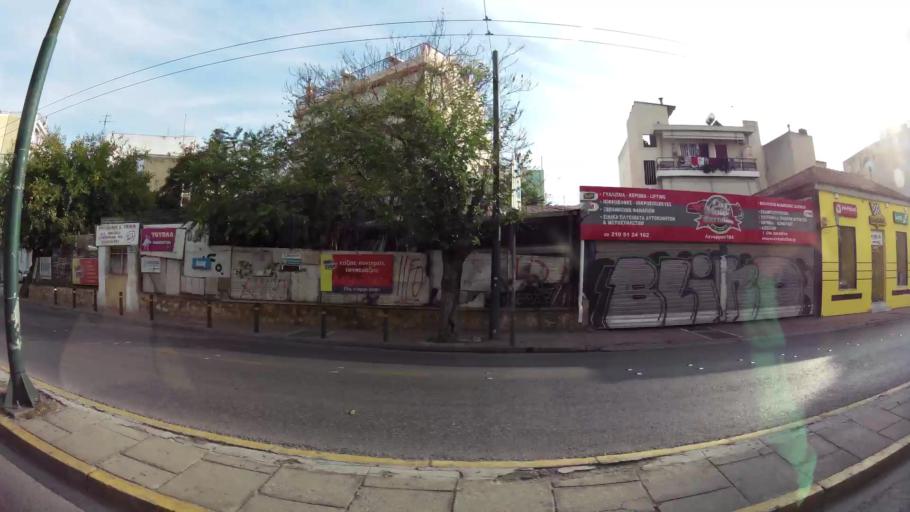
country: GR
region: Attica
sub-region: Nomarchia Athinas
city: Athens
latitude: 37.9954
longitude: 23.7124
